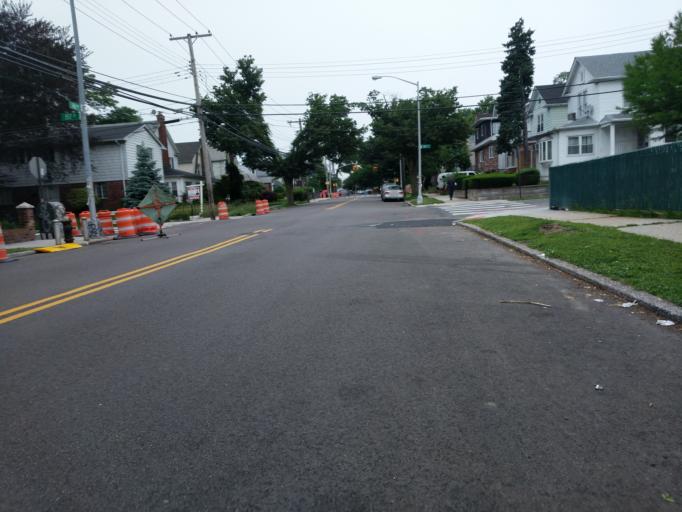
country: US
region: New York
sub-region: Queens County
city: Jamaica
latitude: 40.7541
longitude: -73.8092
